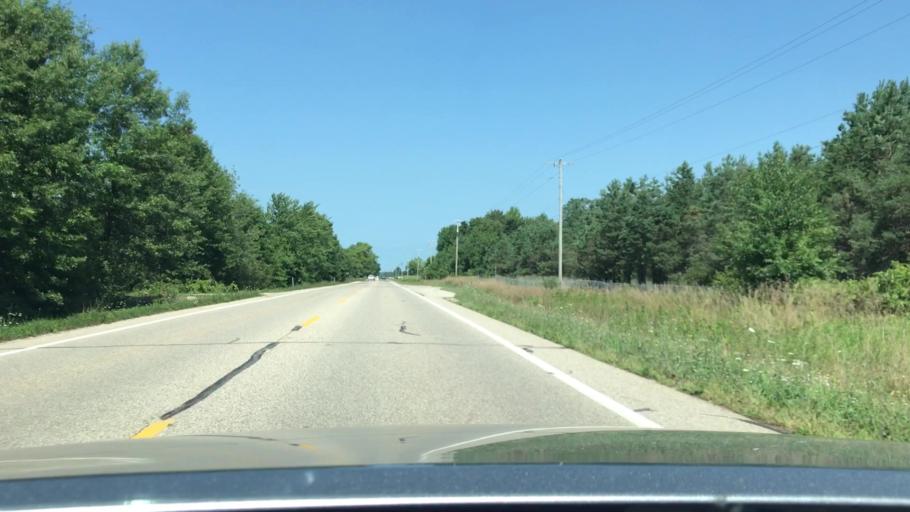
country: US
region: Michigan
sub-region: Ottawa County
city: Allendale
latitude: 42.9467
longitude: -86.0821
